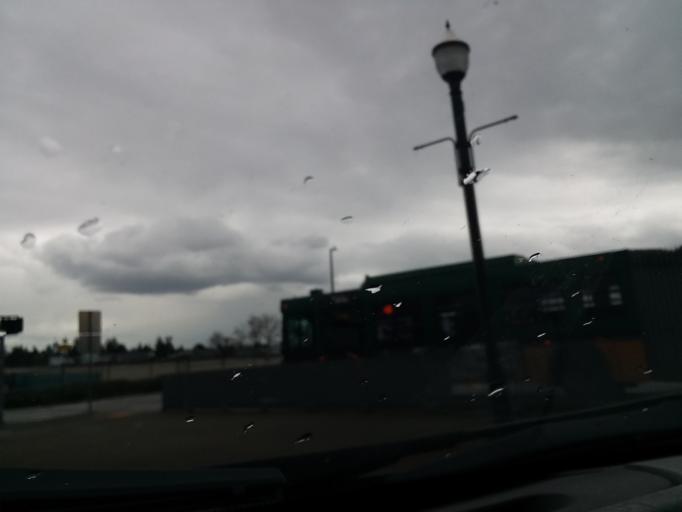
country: US
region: Washington
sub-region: King County
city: Burien
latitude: 47.4704
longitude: -122.3372
